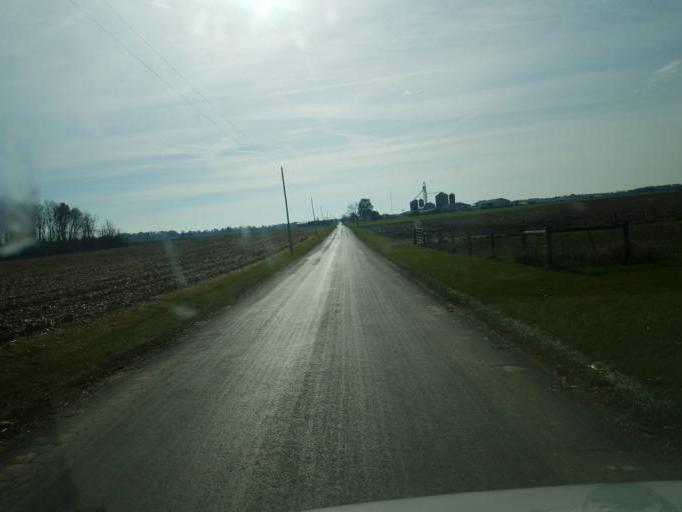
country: US
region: Ohio
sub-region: Hardin County
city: Kenton
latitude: 40.6038
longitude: -83.4425
